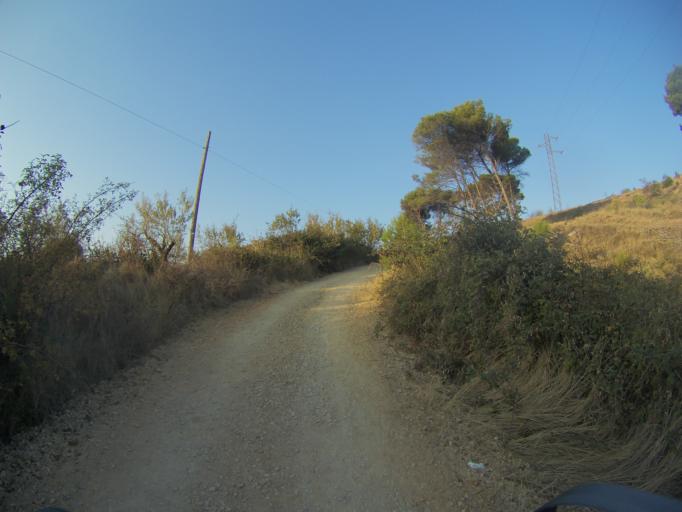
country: ES
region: Navarre
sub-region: Provincia de Navarra
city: Bargota
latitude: 42.5273
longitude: -2.3250
